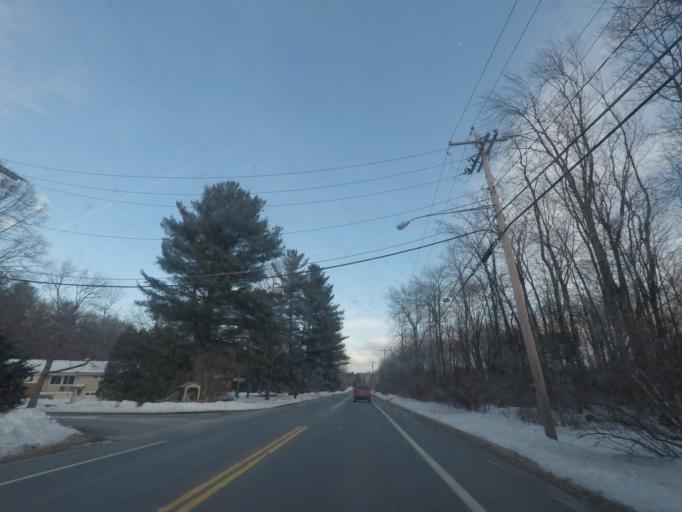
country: US
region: New York
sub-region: Schenectady County
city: Niskayuna
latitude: 42.8359
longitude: -73.8280
